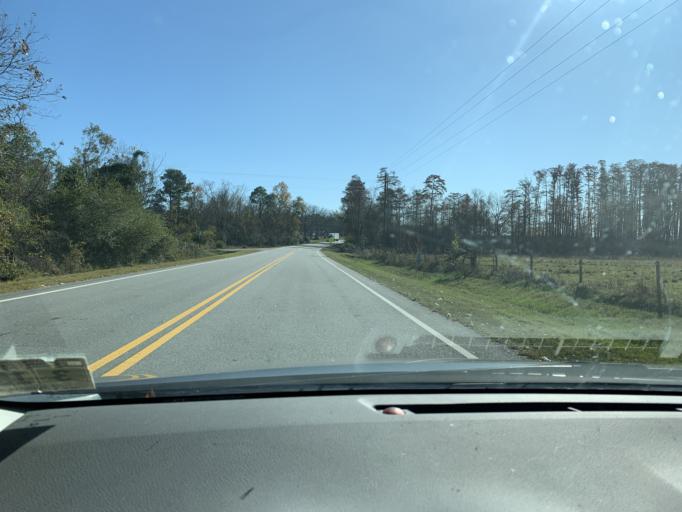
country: US
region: Georgia
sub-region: Ben Hill County
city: Fitzgerald
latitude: 31.7130
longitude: -83.1711
